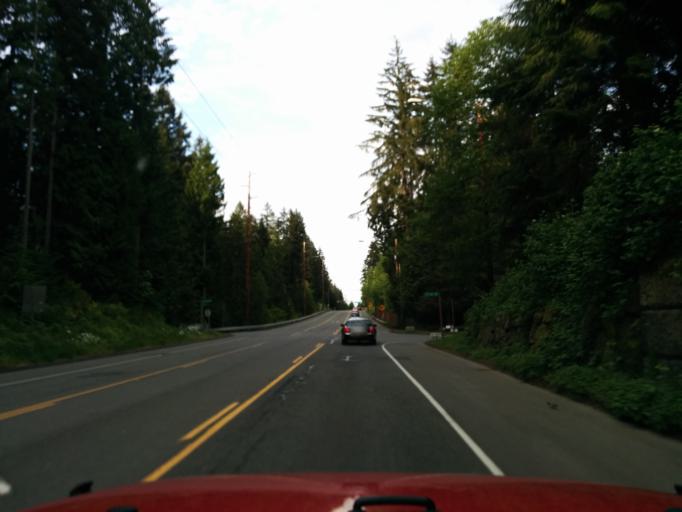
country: US
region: Washington
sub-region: King County
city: Union Hill-Novelty Hill
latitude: 47.6934
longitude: -122.0501
